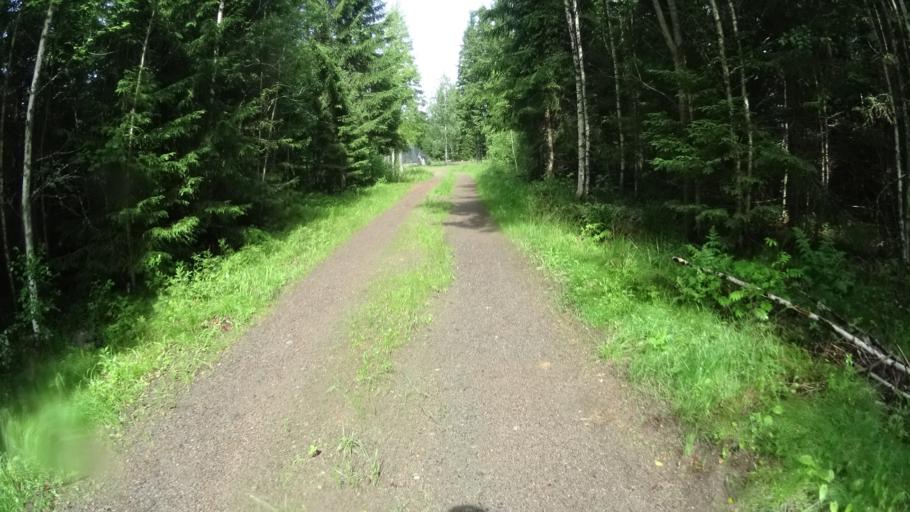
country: FI
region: Uusimaa
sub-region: Helsinki
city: Karkkila
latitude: 60.5886
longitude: 24.3319
